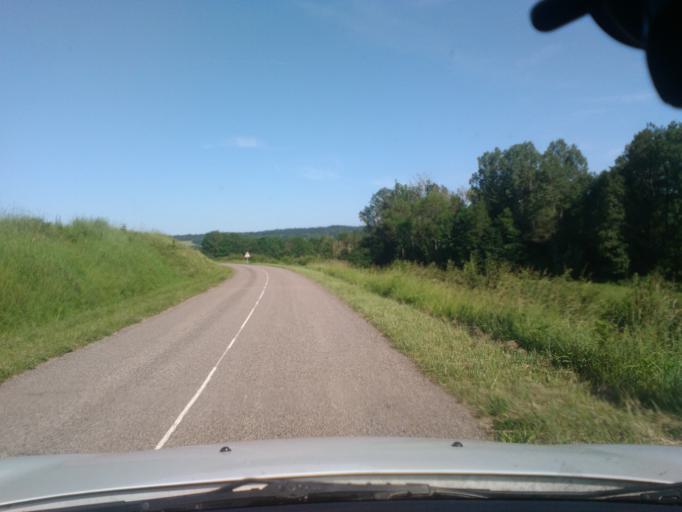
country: FR
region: Lorraine
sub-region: Departement des Vosges
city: Mirecourt
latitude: 48.2676
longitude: 6.2069
